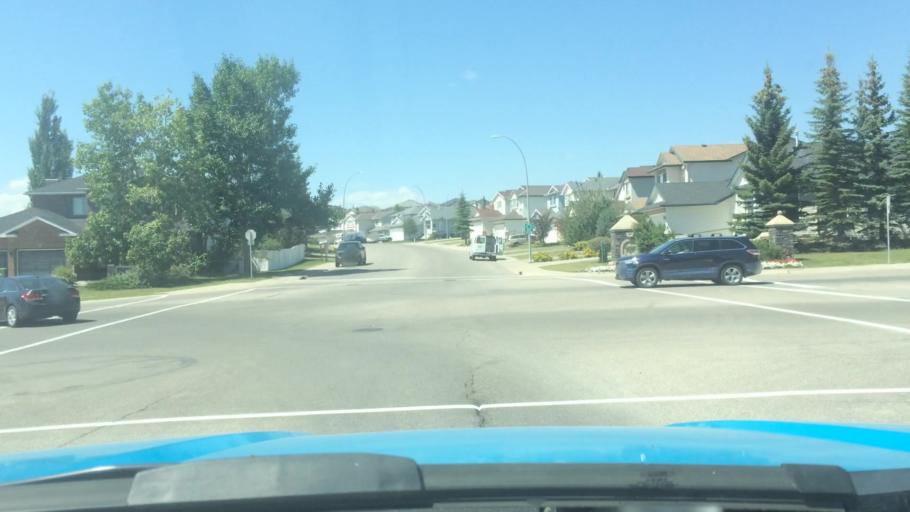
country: CA
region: Alberta
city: Calgary
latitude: 51.1357
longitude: -114.2010
